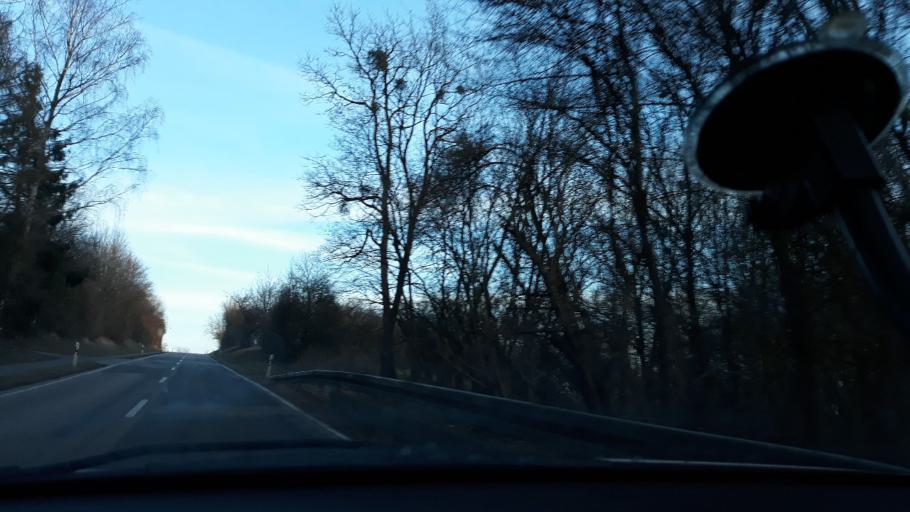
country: DE
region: Saarland
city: Sankt Ingbert
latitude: 49.2222
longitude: 7.1466
